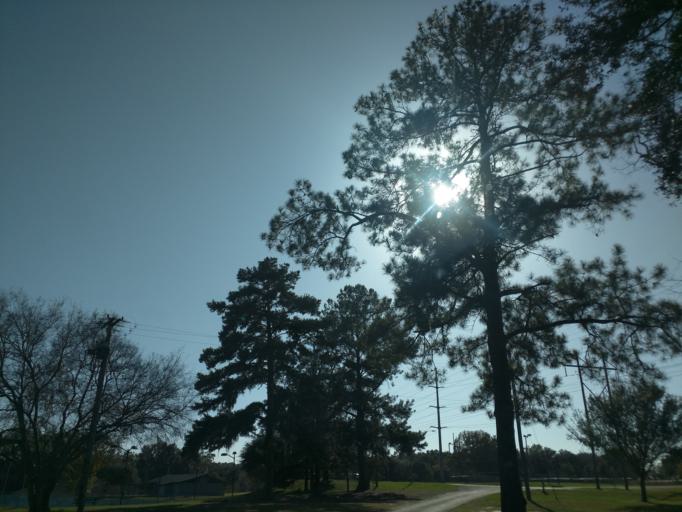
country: US
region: Florida
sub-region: Leon County
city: Tallahassee
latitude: 30.4453
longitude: -84.2157
